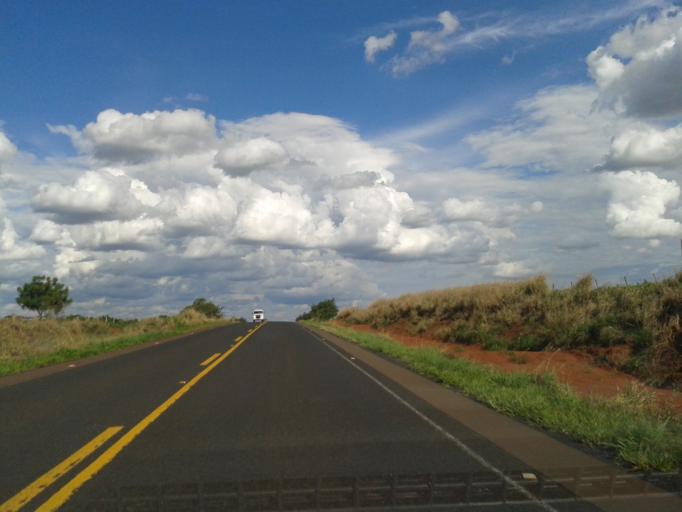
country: BR
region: Minas Gerais
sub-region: Campina Verde
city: Campina Verde
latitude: -19.5567
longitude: -49.8359
